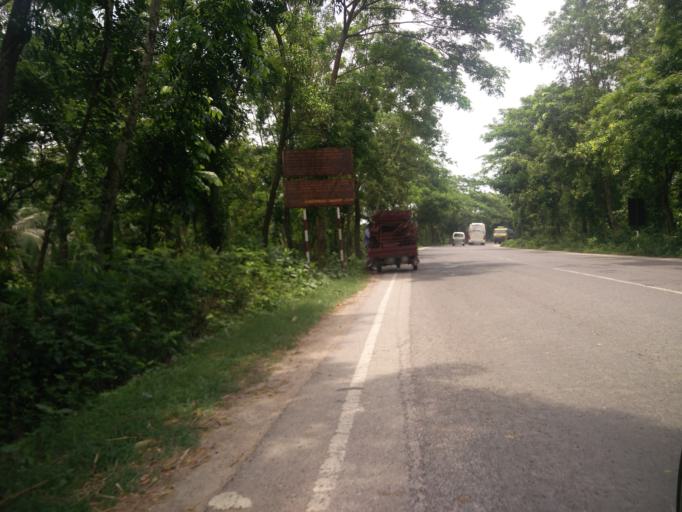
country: BD
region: Khulna
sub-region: Magura
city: Magura
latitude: 23.5451
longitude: 89.5186
